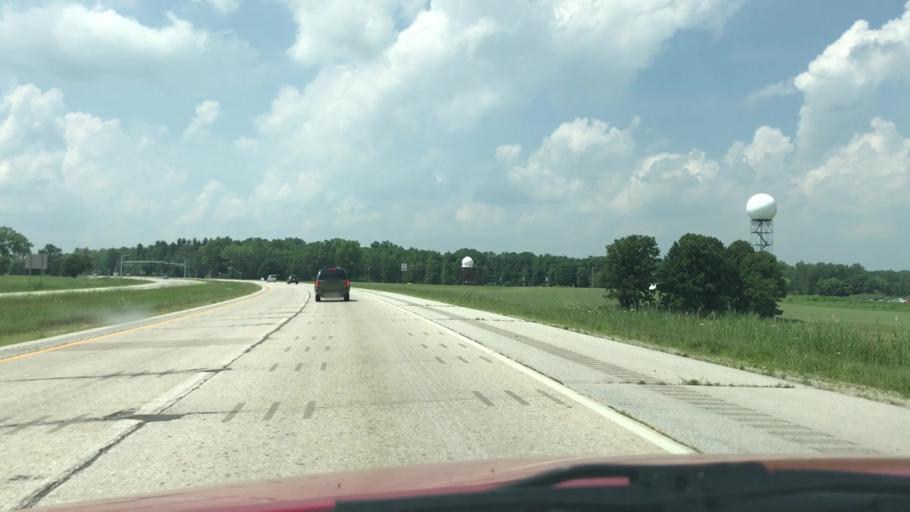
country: US
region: Wisconsin
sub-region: Brown County
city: Ashwaubenon
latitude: 44.4961
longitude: -88.1079
